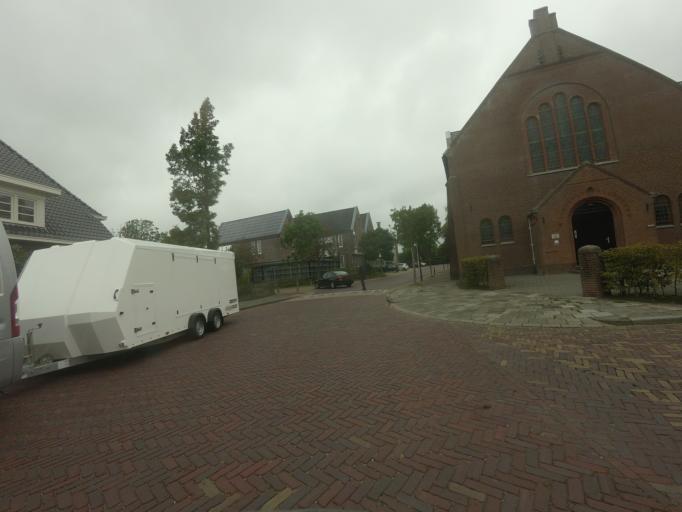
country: NL
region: Friesland
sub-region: Gemeente Ferwerderadiel
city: Ferwert
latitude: 53.3371
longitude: 5.8244
